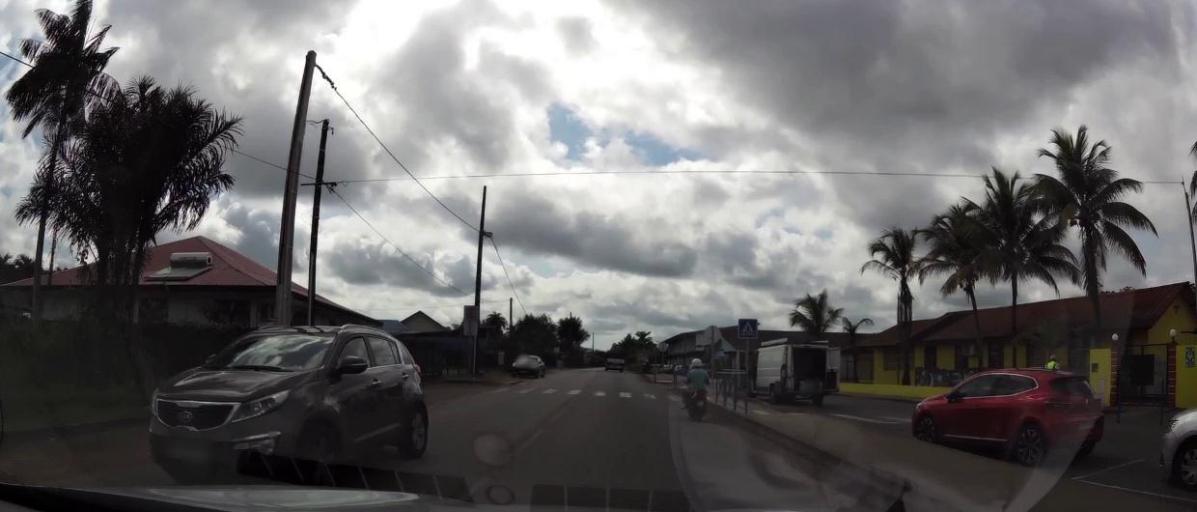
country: GF
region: Guyane
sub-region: Guyane
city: Matoury
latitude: 4.8744
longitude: -52.3303
